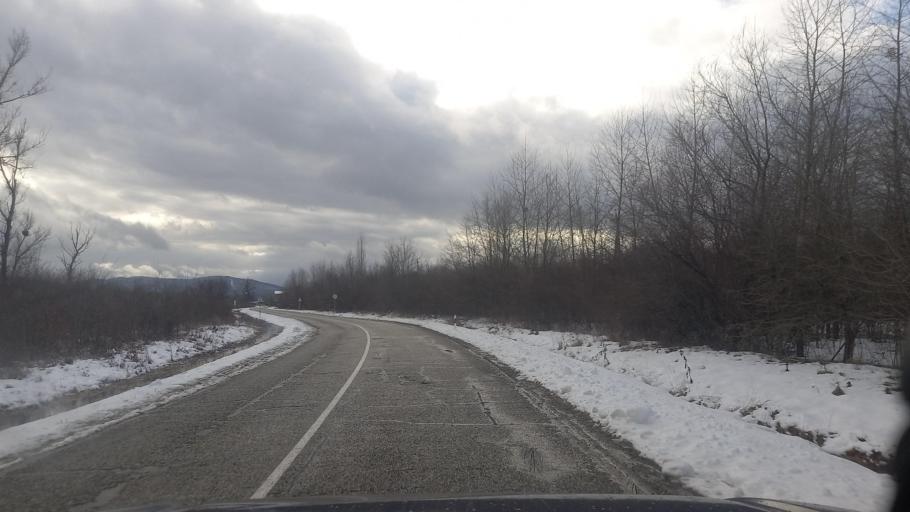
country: RU
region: Krasnodarskiy
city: Smolenskaya
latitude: 44.7559
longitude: 38.8450
